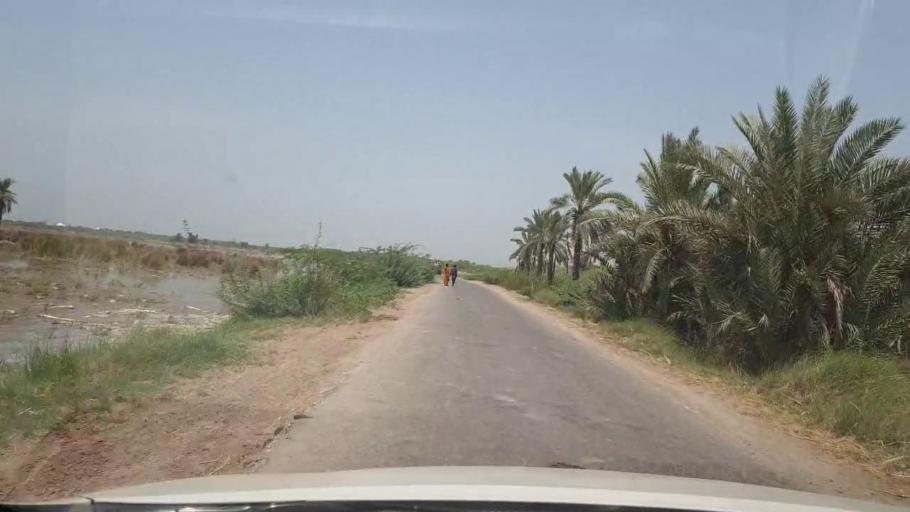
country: PK
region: Sindh
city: Bozdar
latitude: 27.2500
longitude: 68.6492
